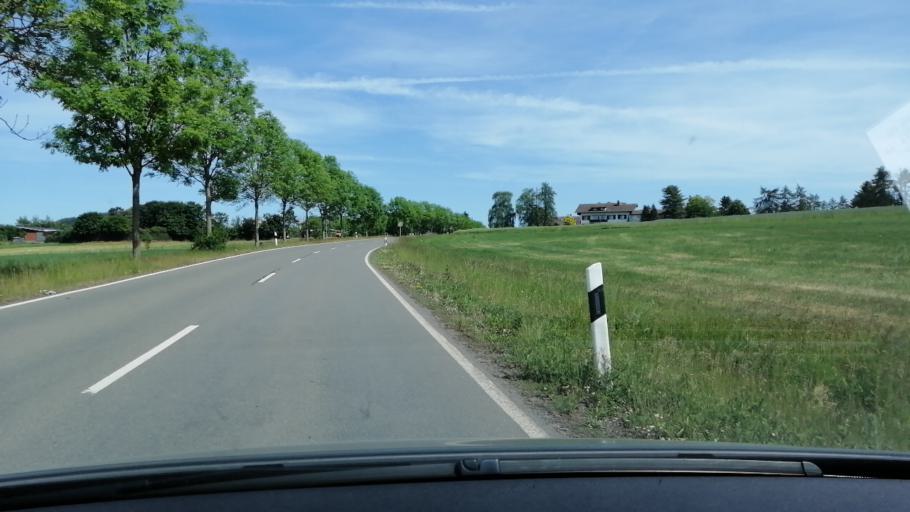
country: DE
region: Hesse
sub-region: Regierungsbezirk Kassel
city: Waldeck
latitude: 51.1796
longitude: 9.0336
